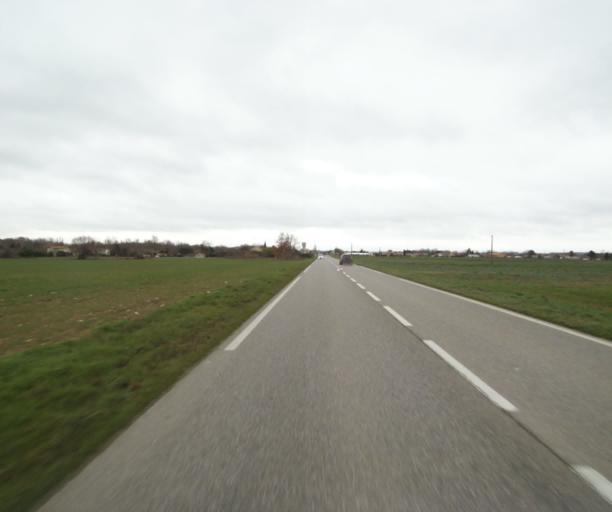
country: FR
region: Midi-Pyrenees
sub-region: Departement de l'Ariege
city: Pamiers
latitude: 43.1802
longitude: 1.6078
